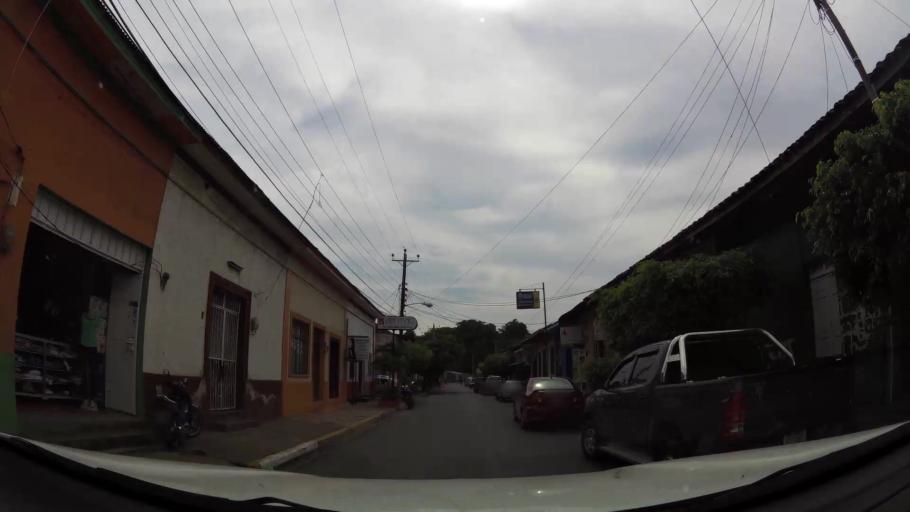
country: NI
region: Rivas
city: Rivas
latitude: 11.4390
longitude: -85.8326
